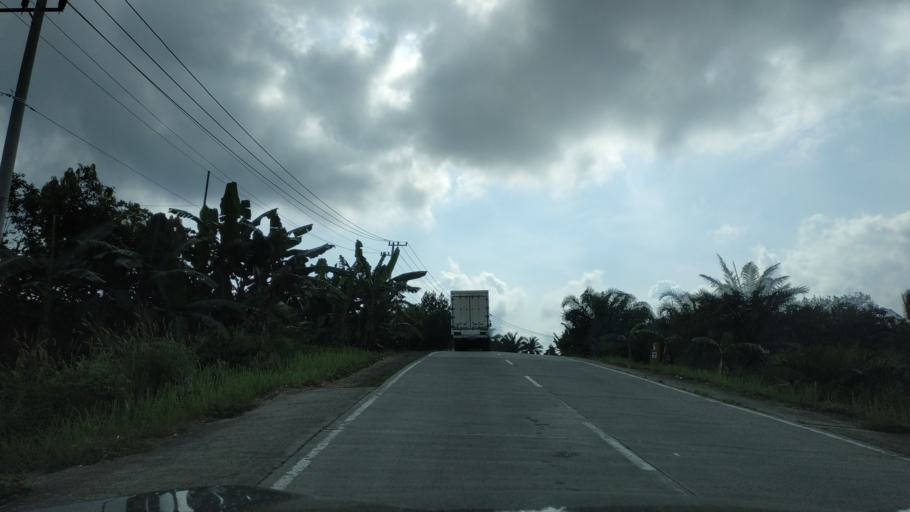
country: ID
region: Riau
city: Pangkalan Kasai
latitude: -0.6966
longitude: 102.4876
